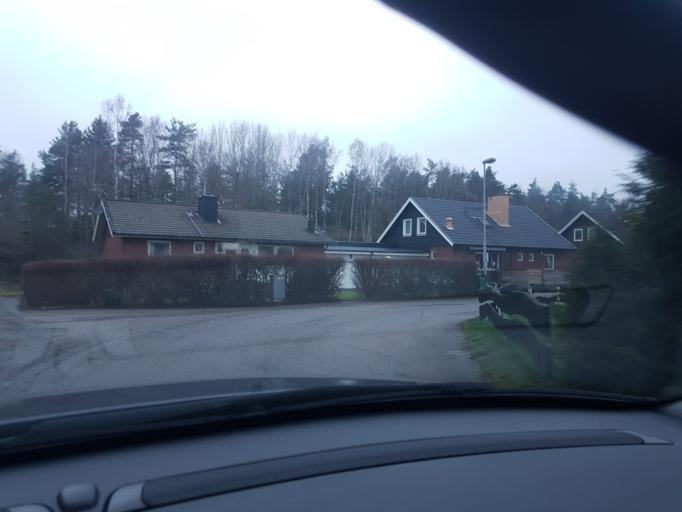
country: SE
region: Vaestra Goetaland
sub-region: Ale Kommun
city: Alvangen
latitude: 57.9538
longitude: 12.1320
